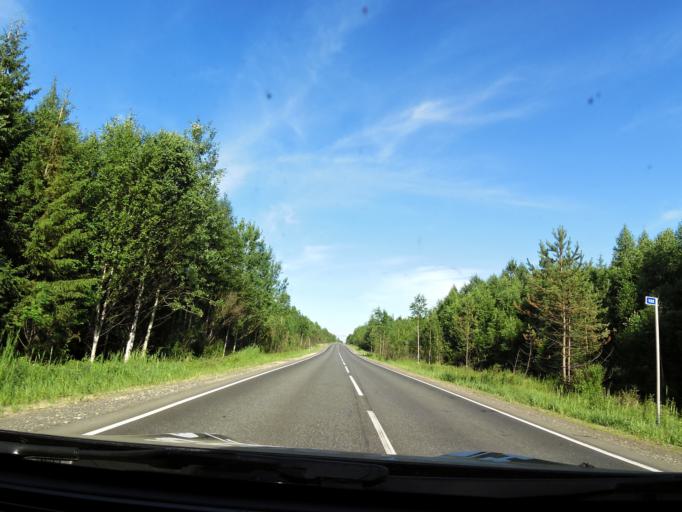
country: RU
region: Kirov
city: Chernaya Kholunitsa
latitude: 58.8745
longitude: 51.4932
